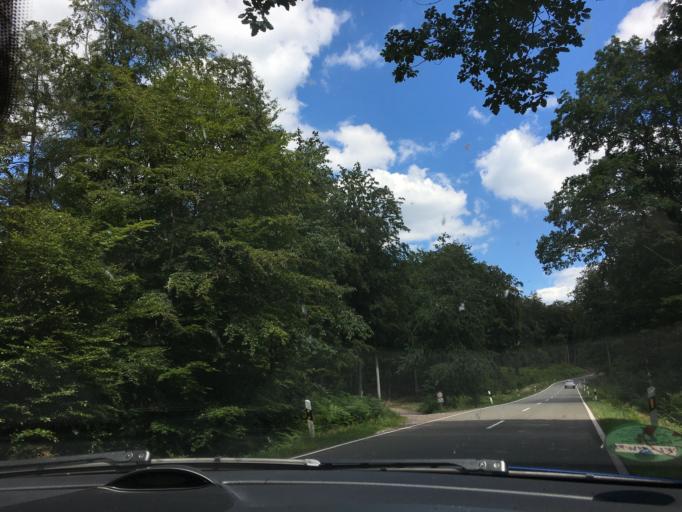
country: DE
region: Rheinland-Pfalz
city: Leimen
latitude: 49.2886
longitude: 7.8254
